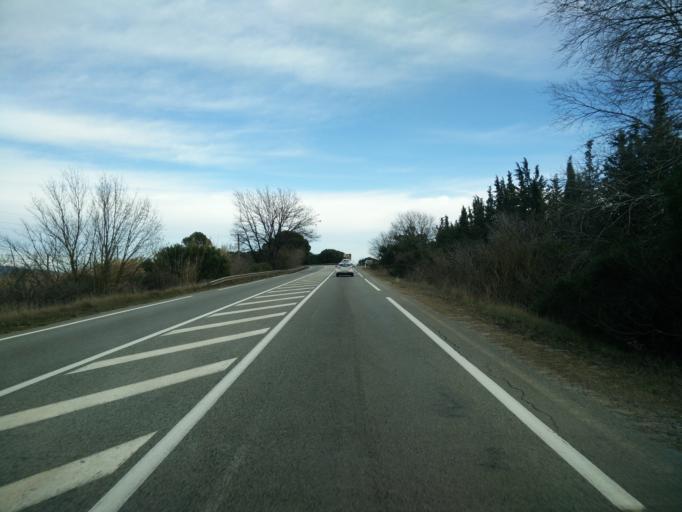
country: FR
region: Provence-Alpes-Cote d'Azur
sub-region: Departement du Var
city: Les Arcs
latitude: 43.4538
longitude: 6.5083
